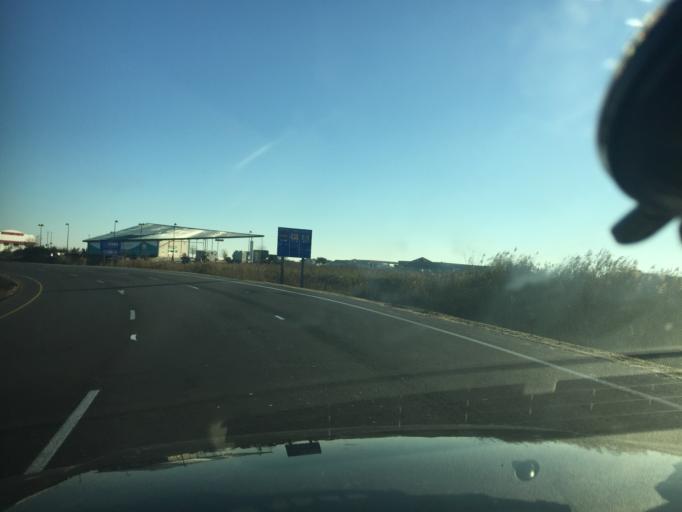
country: US
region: Louisiana
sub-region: Saint Tammany Parish
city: Eden Isle
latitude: 30.2190
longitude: -89.7830
